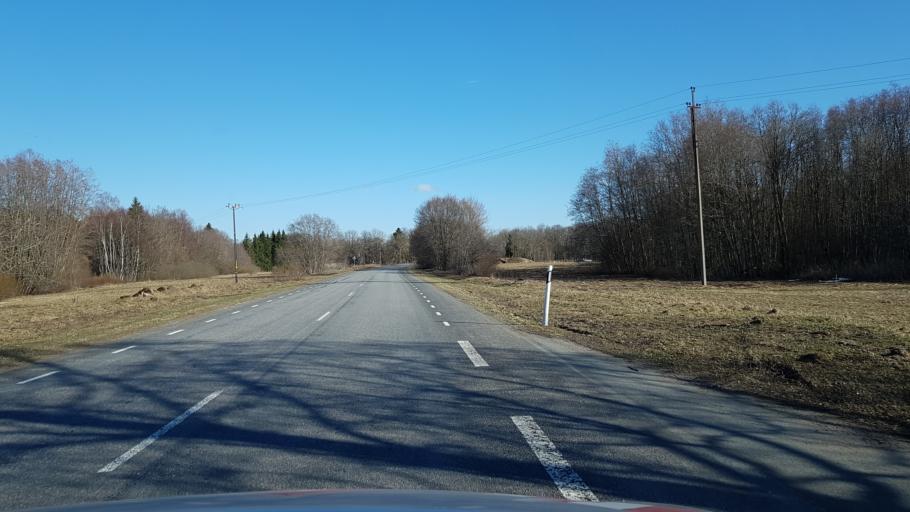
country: EE
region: Laeaene-Virumaa
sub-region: Haljala vald
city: Haljala
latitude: 59.4557
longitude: 26.2311
